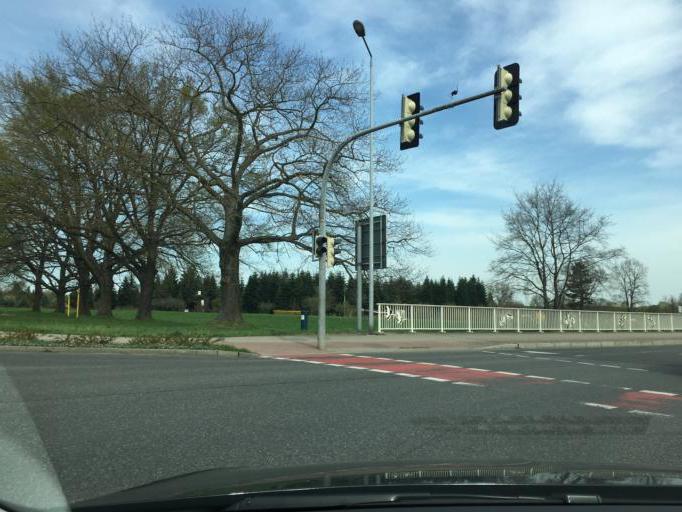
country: DE
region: Saxony
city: Hoyerswerda
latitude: 51.4422
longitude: 14.2508
